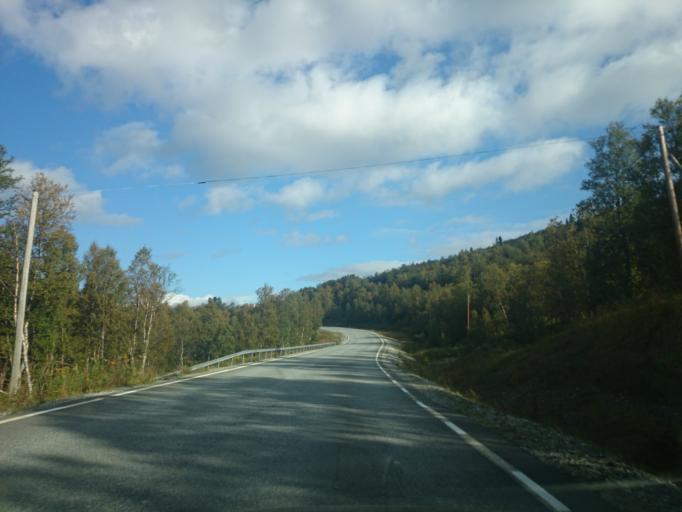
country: NO
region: Sor-Trondelag
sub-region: Tydal
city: Aas
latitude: 62.6656
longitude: 12.4296
